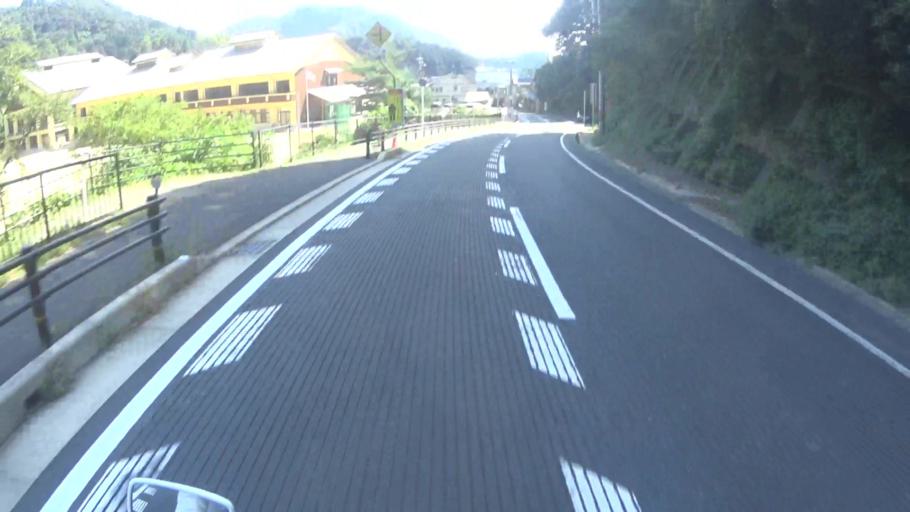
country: JP
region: Kyoto
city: Miyazu
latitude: 35.6787
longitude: 135.2862
